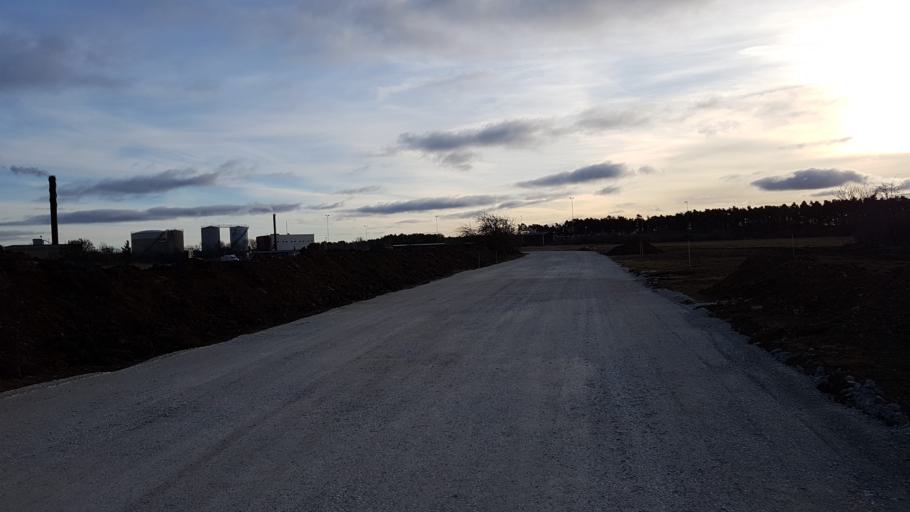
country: SE
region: Gotland
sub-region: Gotland
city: Visby
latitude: 57.6256
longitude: 18.3131
